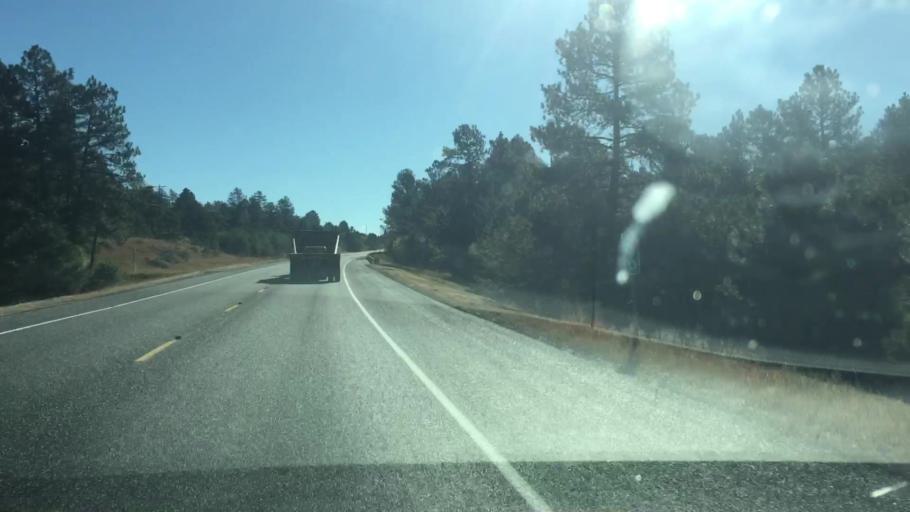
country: US
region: Colorado
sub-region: Elbert County
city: Ponderosa Park
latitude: 39.3777
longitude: -104.6985
